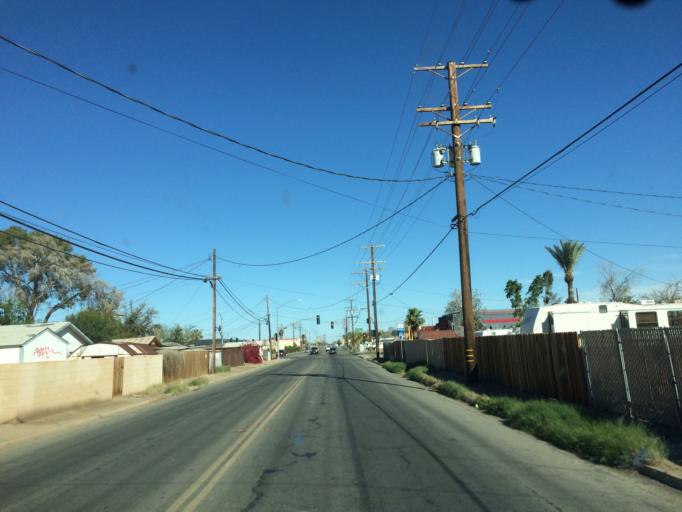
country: US
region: California
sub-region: Imperial County
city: El Centro
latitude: 32.7815
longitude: -115.5538
